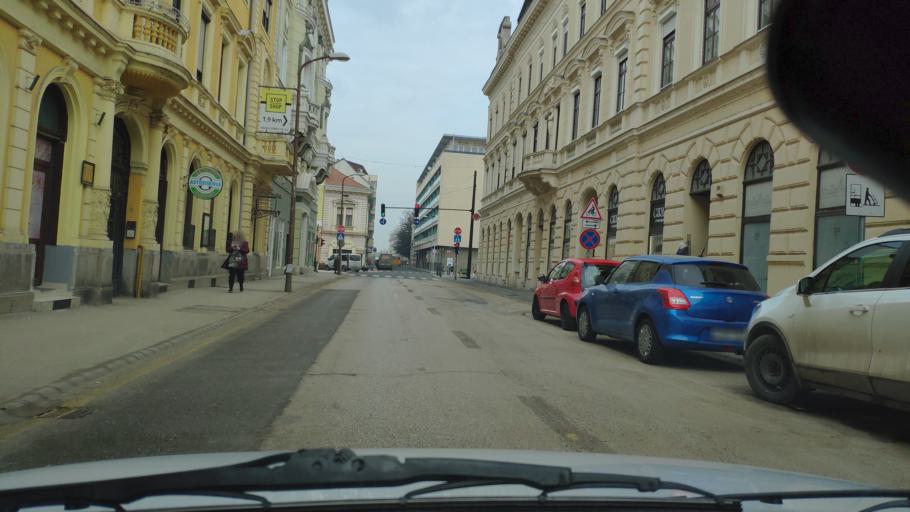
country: HU
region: Zala
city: Nagykanizsa
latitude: 46.4542
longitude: 16.9918
